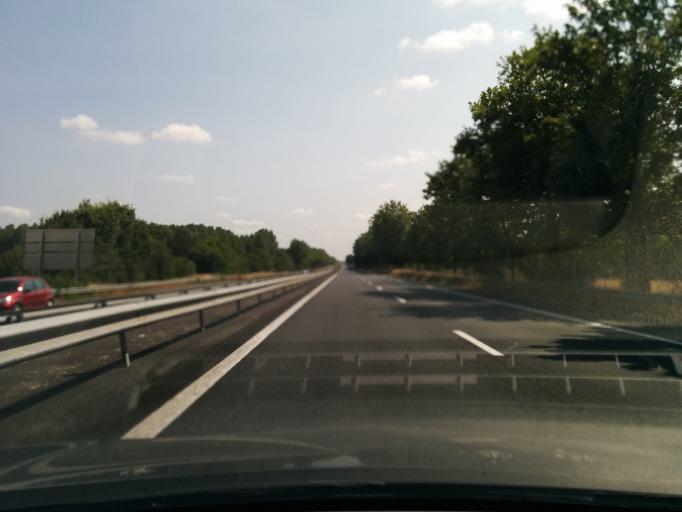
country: FR
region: Centre
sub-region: Departement de l'Indre
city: Montierchaume
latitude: 46.9270
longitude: 1.7447
